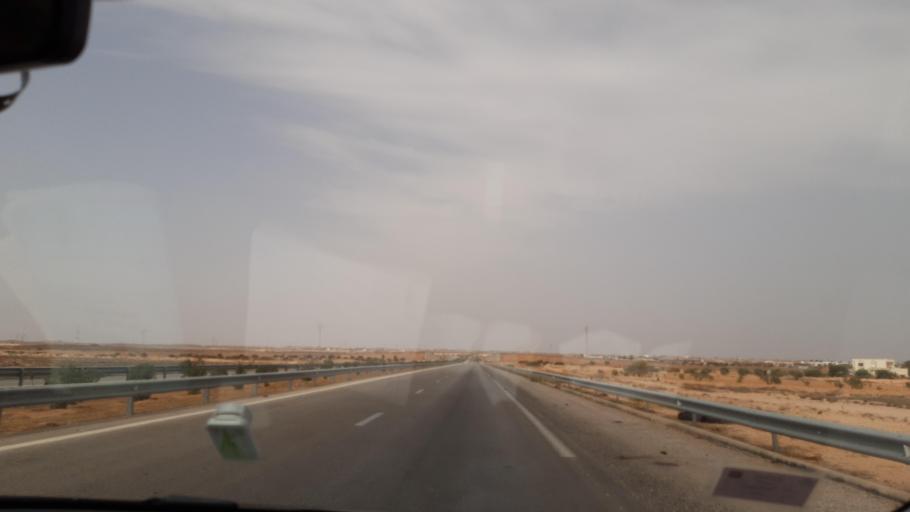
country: TN
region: Safaqis
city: Sfax
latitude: 34.7627
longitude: 10.6087
